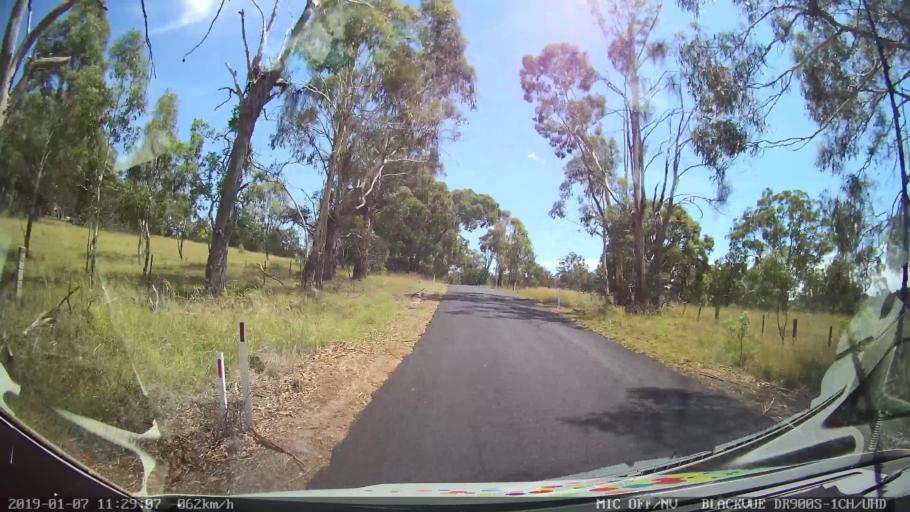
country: AU
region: New South Wales
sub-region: Armidale Dumaresq
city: Armidale
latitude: -30.4419
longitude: 151.5648
